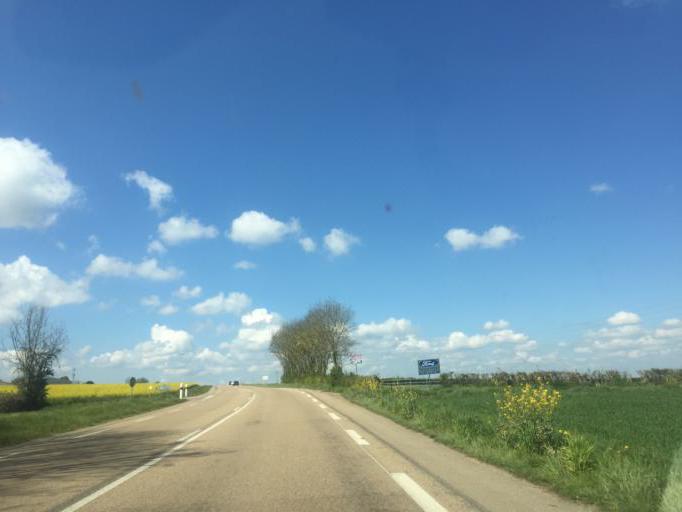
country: FR
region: Bourgogne
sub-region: Departement de l'Yonne
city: Avallon
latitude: 47.4966
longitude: 3.9507
